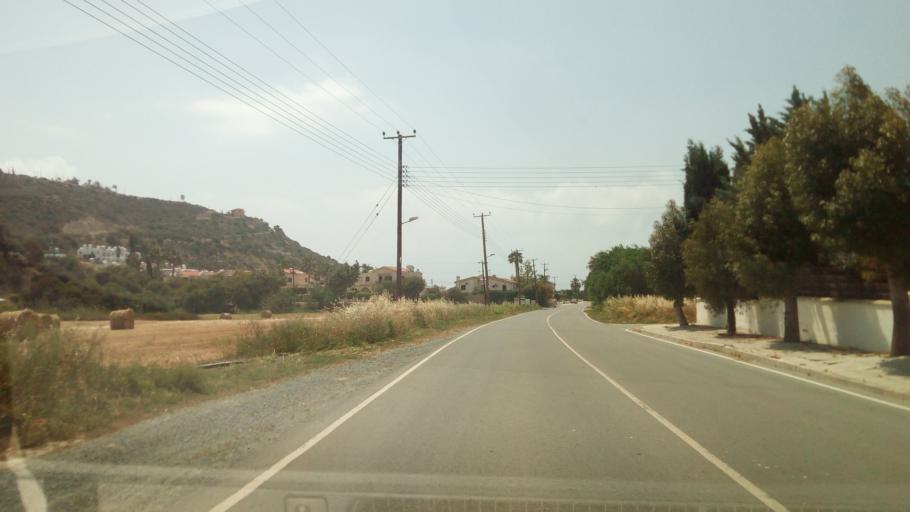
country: CY
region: Limassol
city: Pissouri
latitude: 34.6576
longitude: 32.7282
